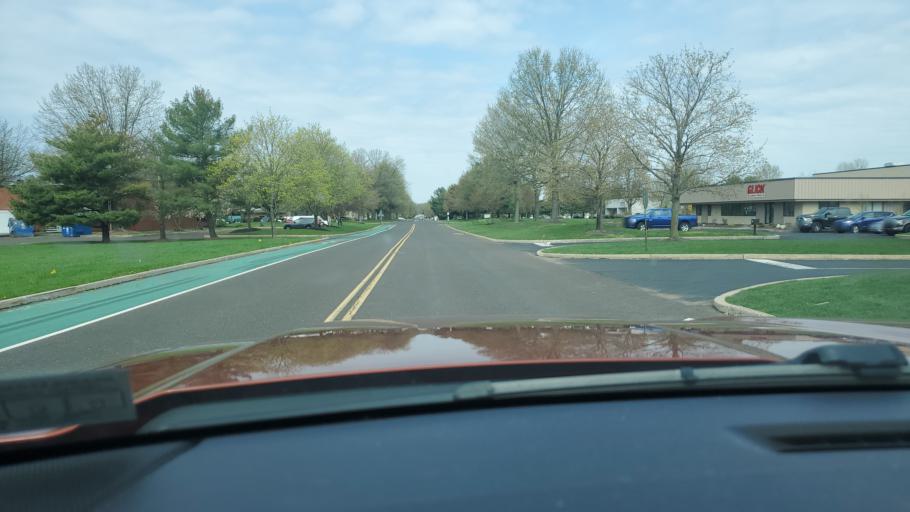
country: US
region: Pennsylvania
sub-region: Montgomery County
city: Hatfield
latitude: 40.2875
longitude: -75.2796
